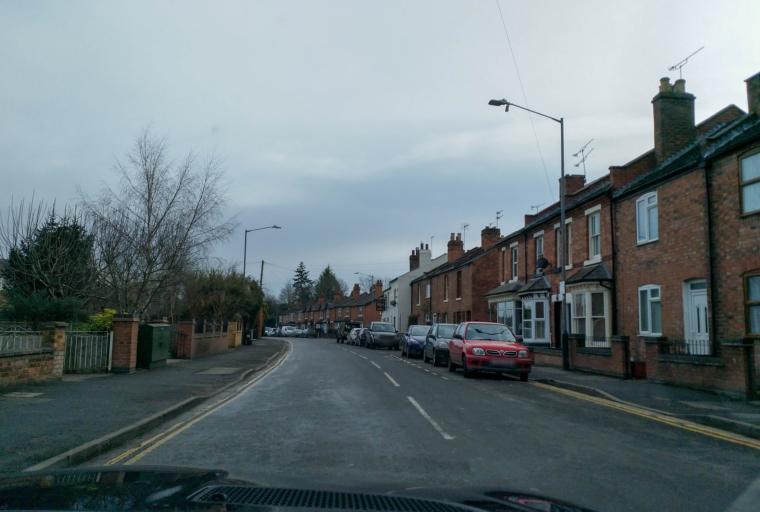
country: GB
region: England
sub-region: Warwickshire
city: Warwick
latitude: 52.2881
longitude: -1.5809
